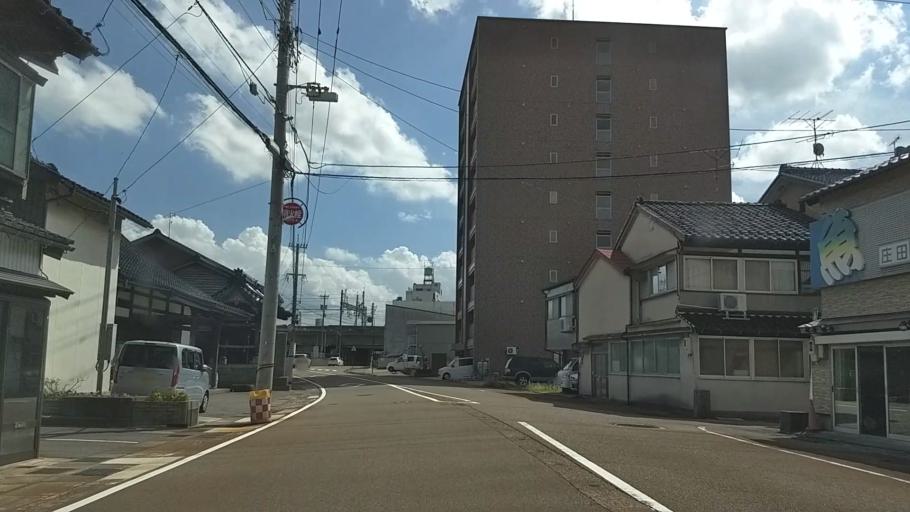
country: JP
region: Ishikawa
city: Kanazawa-shi
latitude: 36.5844
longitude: 136.6519
